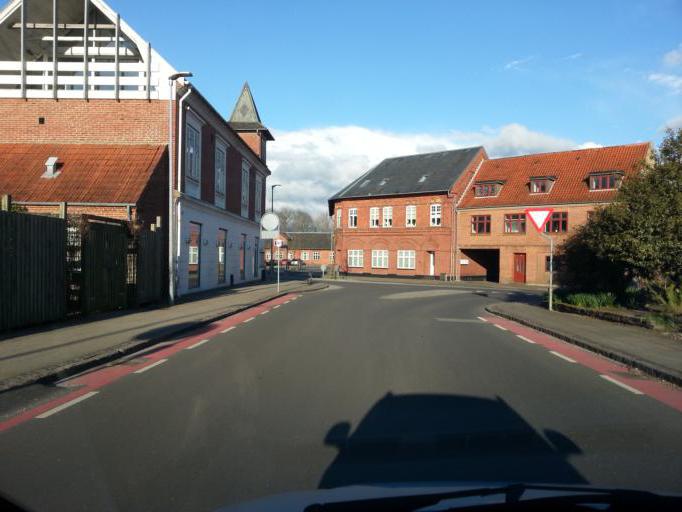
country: DK
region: South Denmark
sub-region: Varde Kommune
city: Olgod
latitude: 55.8107
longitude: 8.6206
